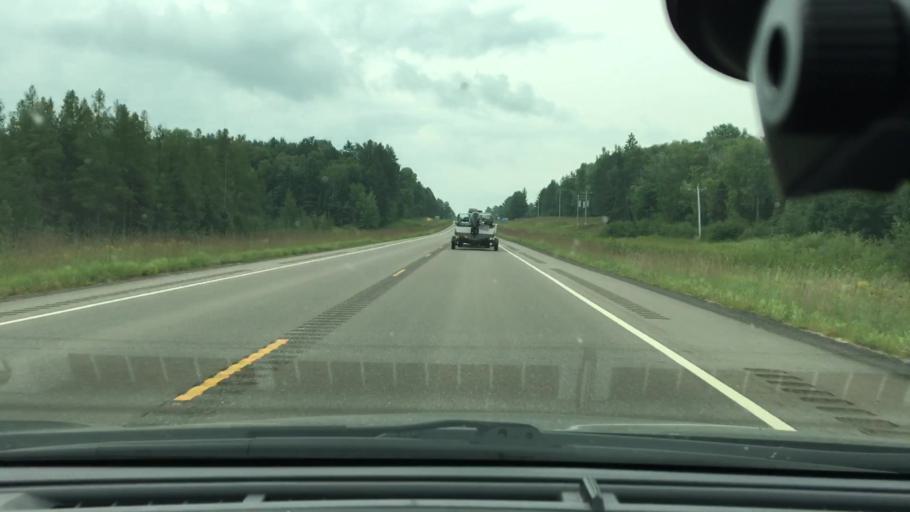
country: US
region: Minnesota
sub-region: Crow Wing County
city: Crosby
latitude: 46.5984
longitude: -93.9527
